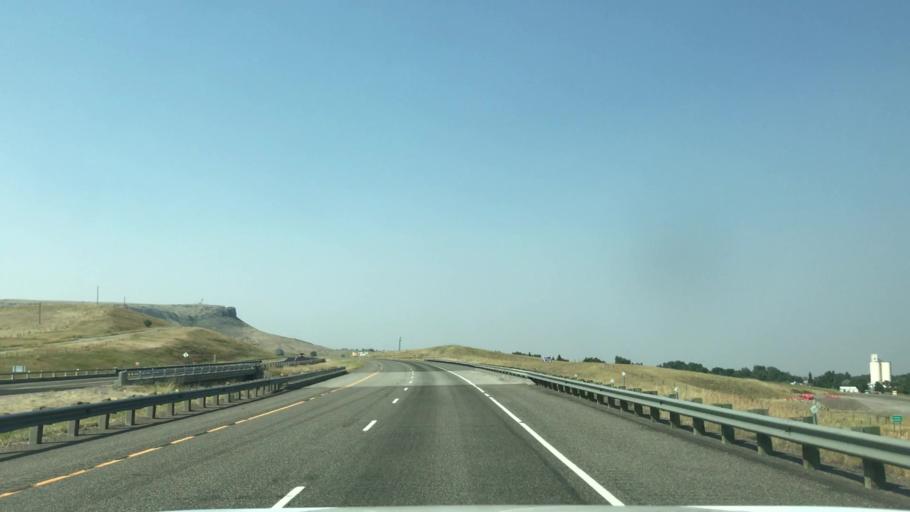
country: US
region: Montana
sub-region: Cascade County
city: Sun Prairie
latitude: 47.2598
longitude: -111.7081
